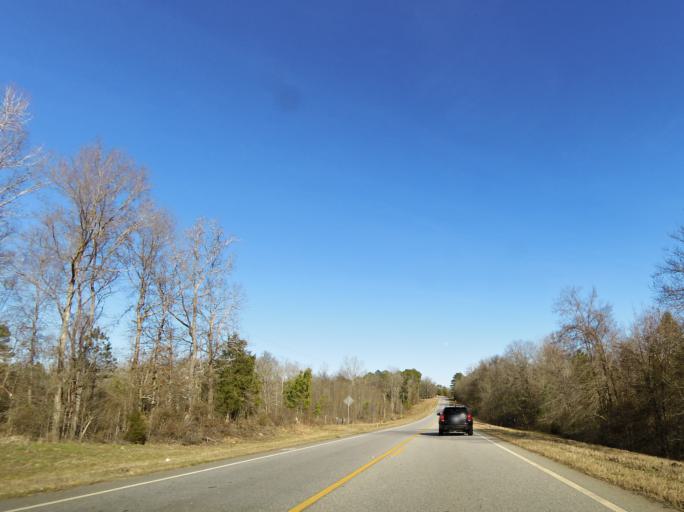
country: US
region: Georgia
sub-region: Crawford County
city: Roberta
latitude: 32.7564
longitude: -84.1383
